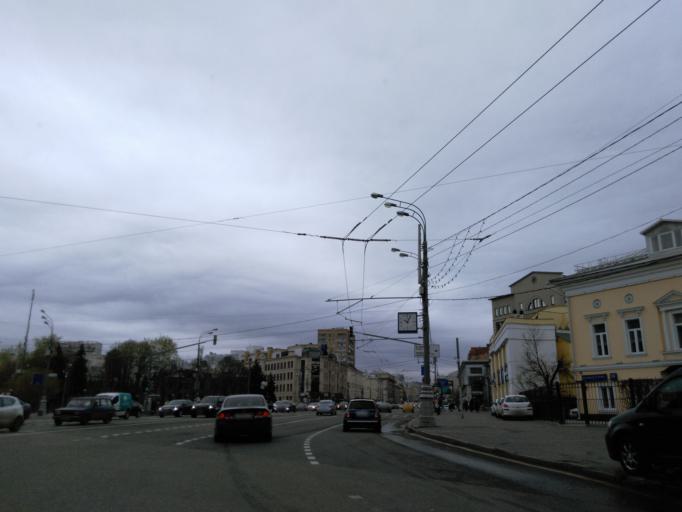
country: RU
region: Moscow
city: Moscow
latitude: 55.7407
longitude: 37.6166
